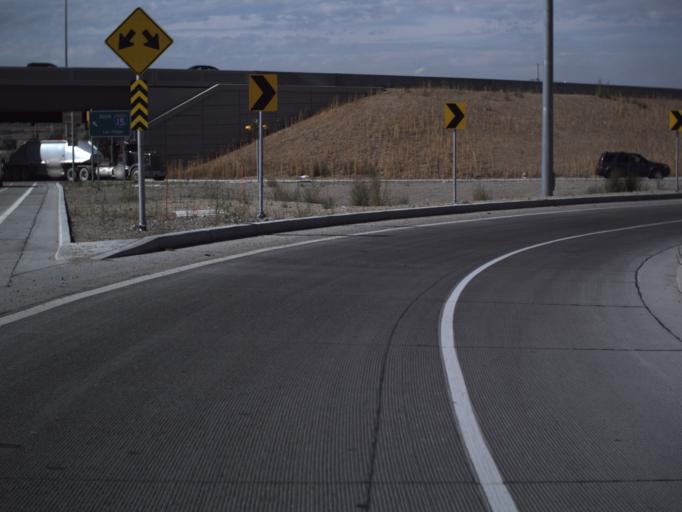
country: US
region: Utah
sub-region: Salt Lake County
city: Bluffdale
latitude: 40.4833
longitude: -111.8977
